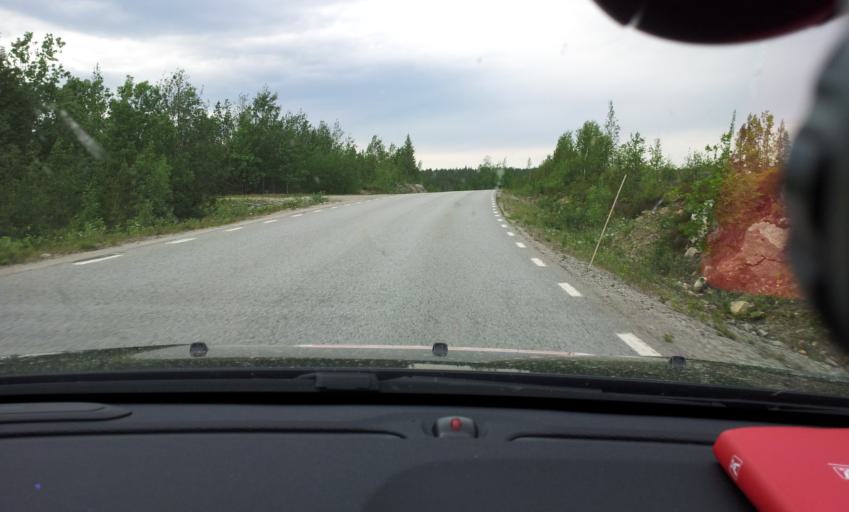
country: SE
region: Jaemtland
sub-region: Bergs Kommun
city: Hoverberg
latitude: 62.6770
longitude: 14.7009
